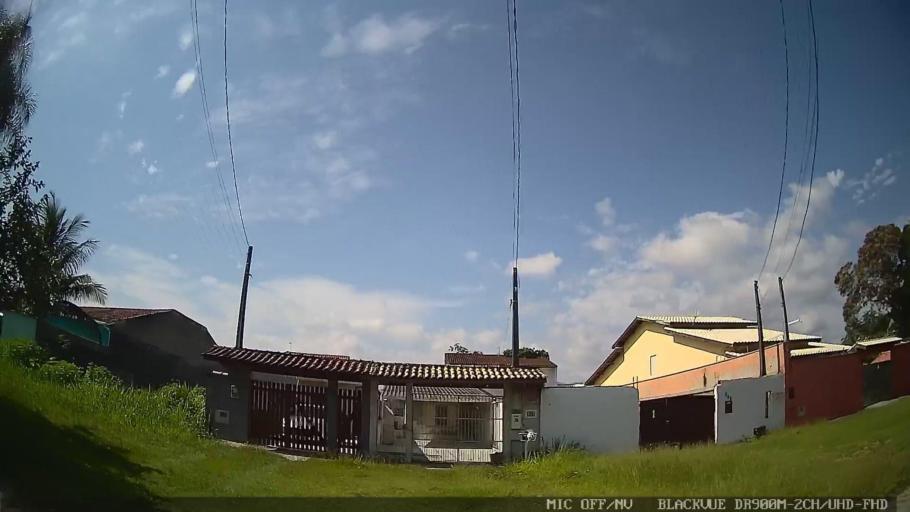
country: BR
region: Sao Paulo
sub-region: Caraguatatuba
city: Caraguatatuba
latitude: -23.6674
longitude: -45.4439
